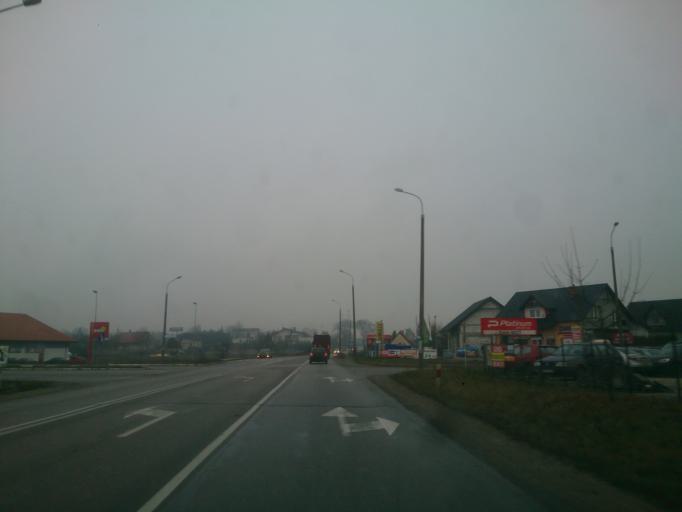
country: PL
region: Pomeranian Voivodeship
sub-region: Powiat starogardzki
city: Zblewo
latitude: 53.9372
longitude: 18.3299
